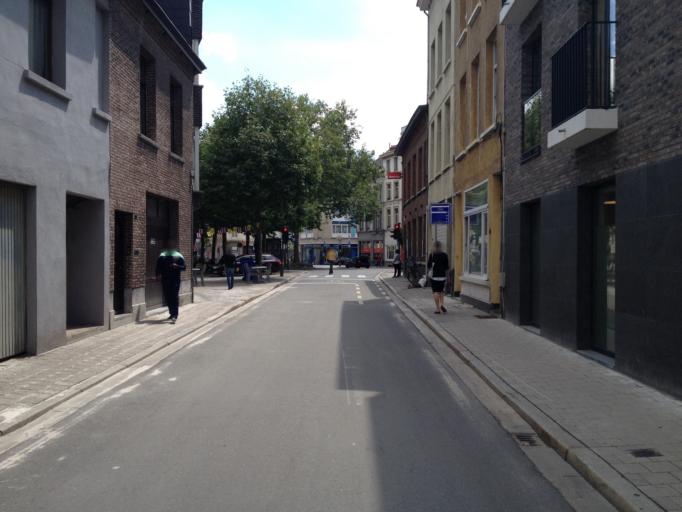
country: BE
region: Flanders
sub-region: Provincie Antwerpen
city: Antwerpen
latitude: 51.2122
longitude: 4.4010
